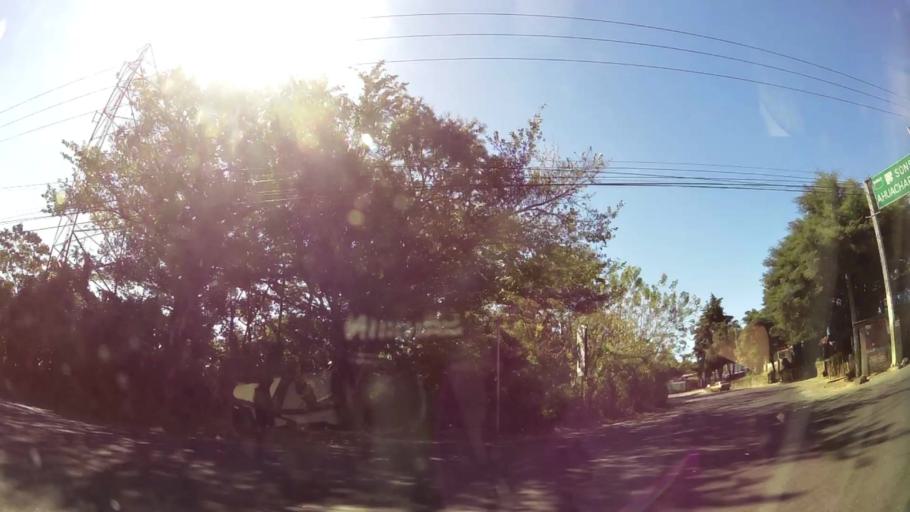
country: SV
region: Sonsonate
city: Juayua
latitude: 13.8322
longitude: -89.7581
